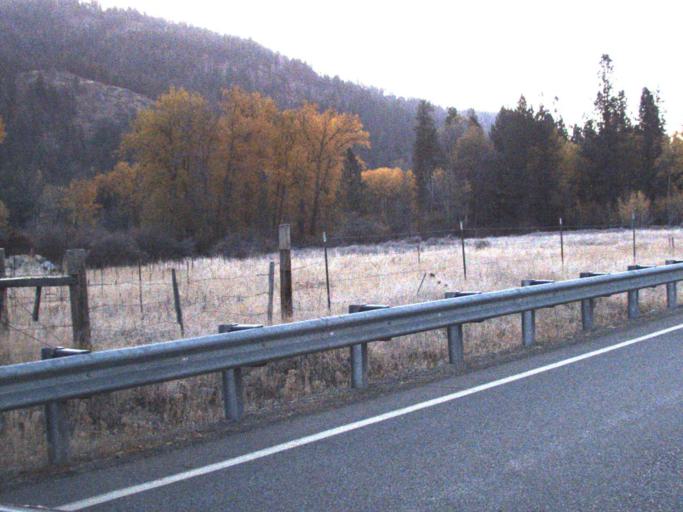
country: US
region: Washington
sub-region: Ferry County
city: Republic
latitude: 48.3006
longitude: -118.7352
